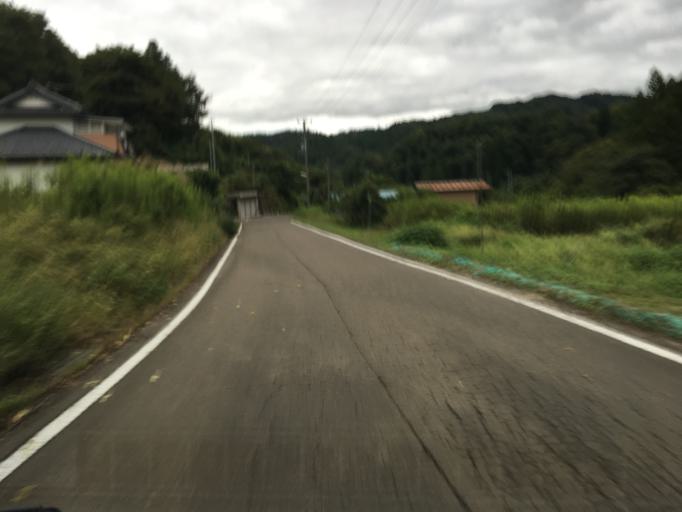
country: JP
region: Fukushima
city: Hobaramachi
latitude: 37.7595
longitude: 140.5408
